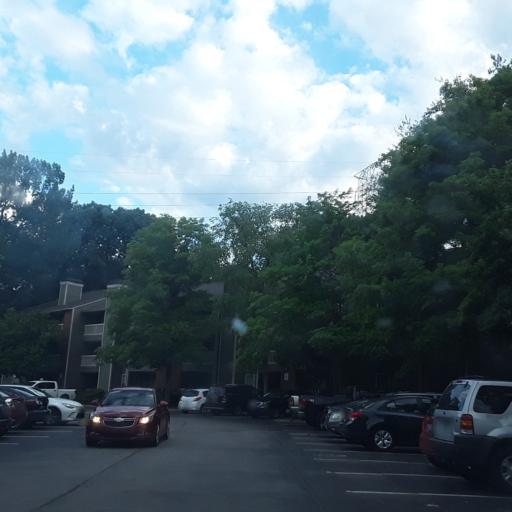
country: US
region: Tennessee
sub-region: Wilson County
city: Green Hill
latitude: 36.1649
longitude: -86.5994
